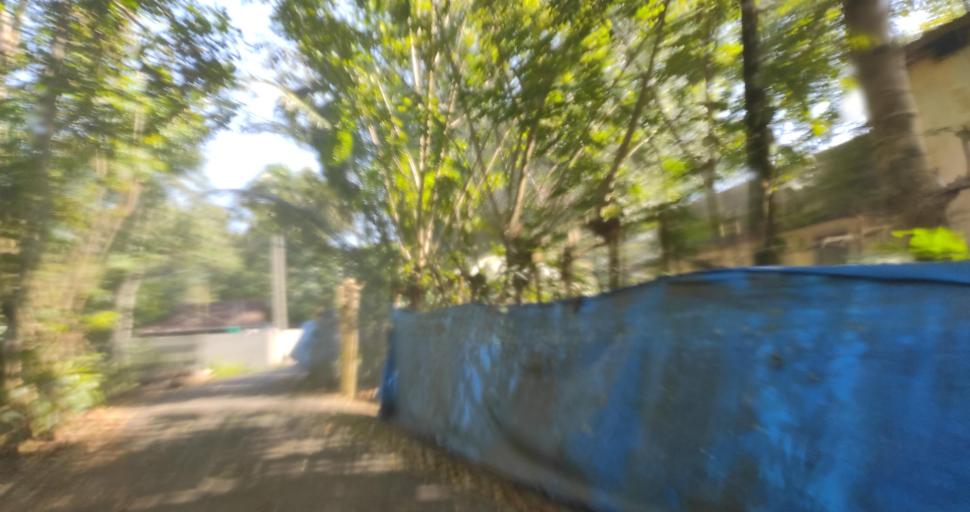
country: IN
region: Kerala
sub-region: Alappuzha
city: Shertallai
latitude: 9.6350
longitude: 76.3408
